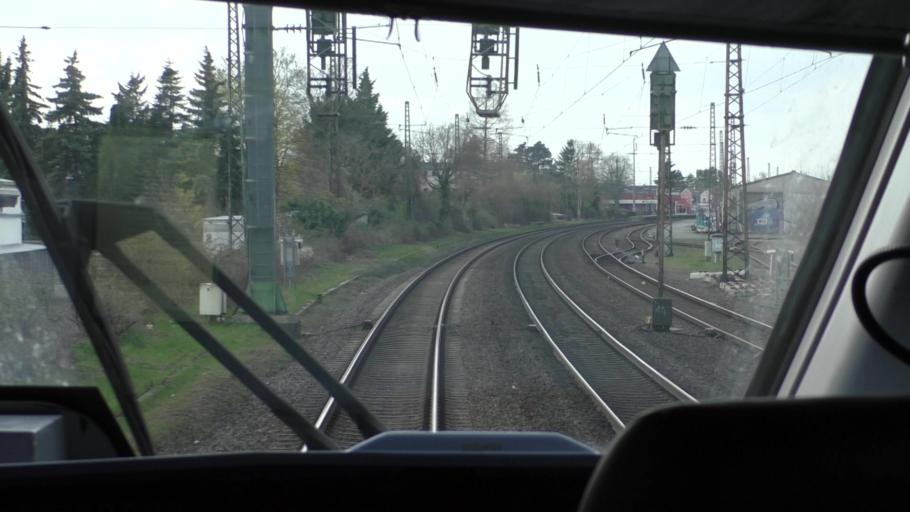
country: DE
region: North Rhine-Westphalia
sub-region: Regierungsbezirk Koln
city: Alfter
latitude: 50.7495
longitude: 7.0240
